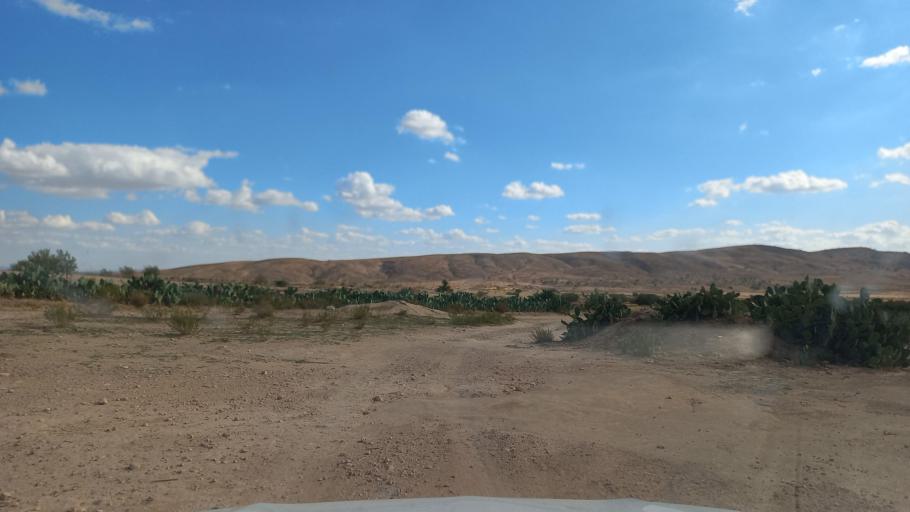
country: TN
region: Al Qasrayn
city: Sbiba
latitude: 35.4016
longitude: 9.0138
